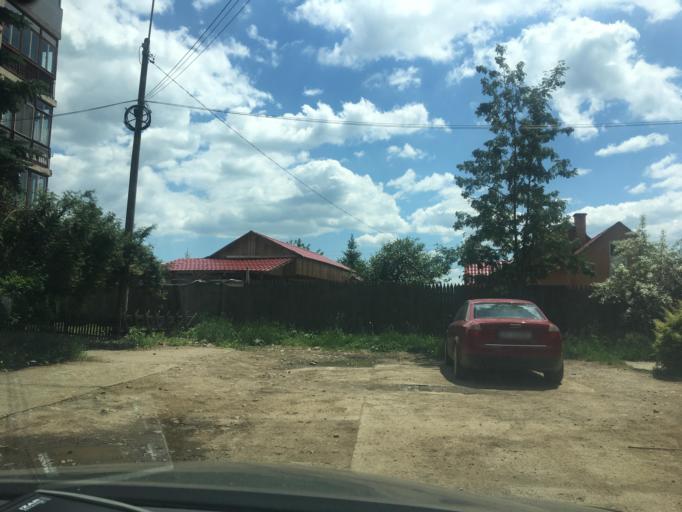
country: RO
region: Harghita
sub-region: Municipiul Gheorgheni
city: Gheorgheni
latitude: 46.7199
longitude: 25.5845
